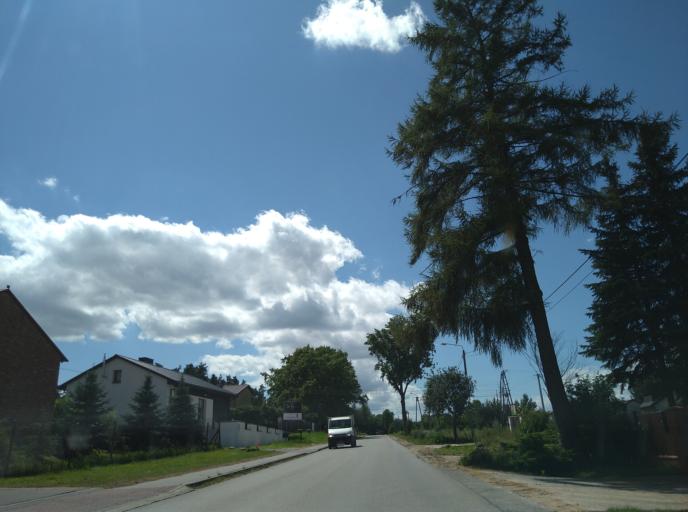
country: PL
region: Masovian Voivodeship
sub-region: Powiat bialobrzeski
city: Promna
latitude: 51.6737
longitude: 20.9396
